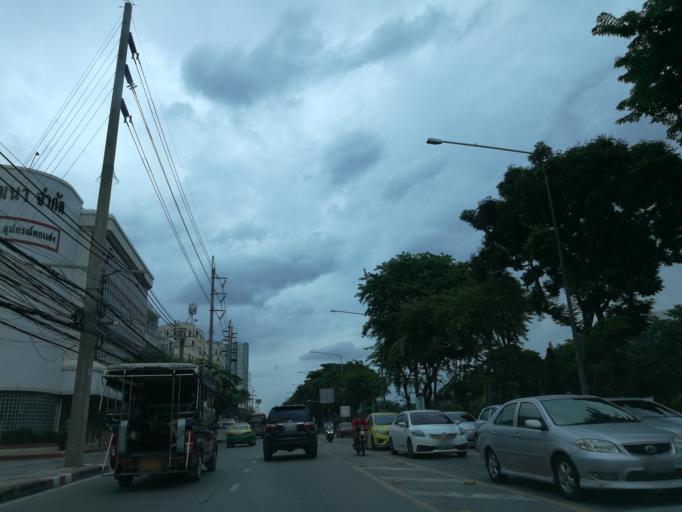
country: TH
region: Bangkok
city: Chatuchak
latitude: 13.8401
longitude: 100.5414
